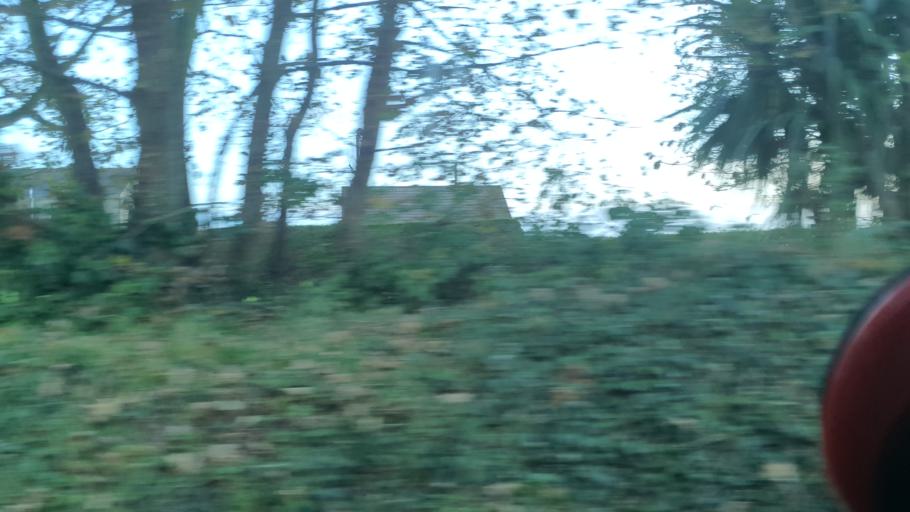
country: GB
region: Northern Ireland
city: Kilkeel
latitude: 54.0409
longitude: -6.0687
